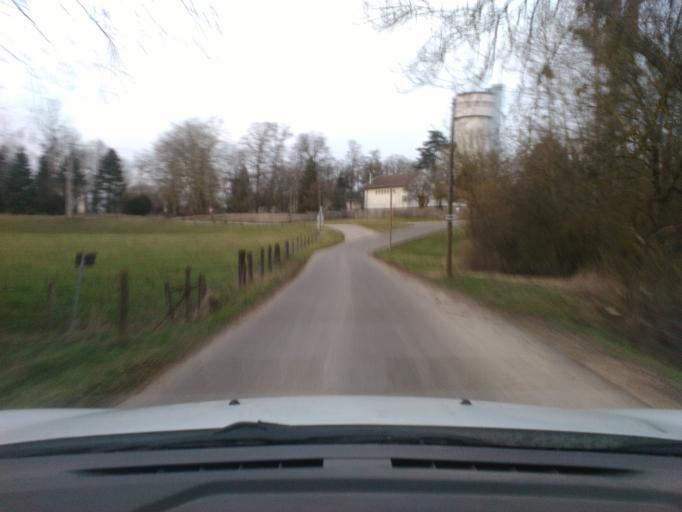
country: FR
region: Lorraine
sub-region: Departement des Vosges
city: Mirecourt
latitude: 48.2882
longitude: 6.1087
